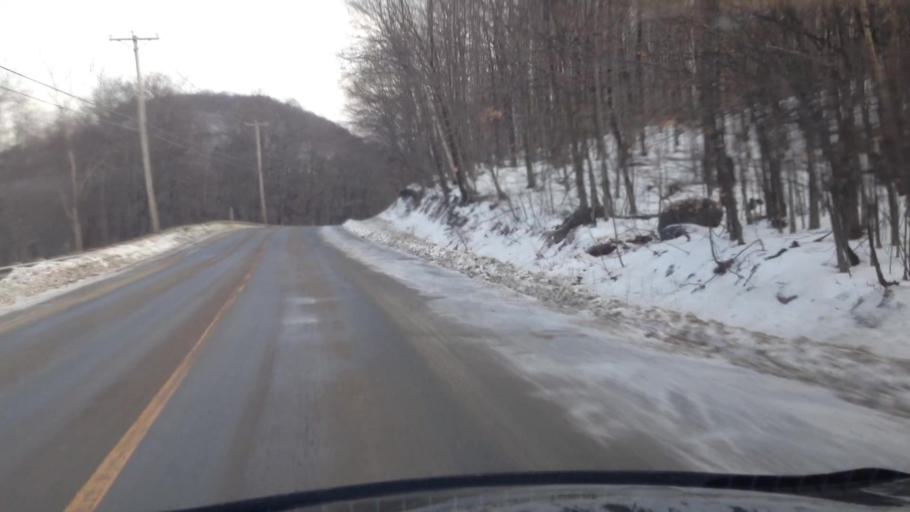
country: CA
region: Quebec
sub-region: Laurentides
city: Brownsburg-Chatham
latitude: 45.9228
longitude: -74.5135
